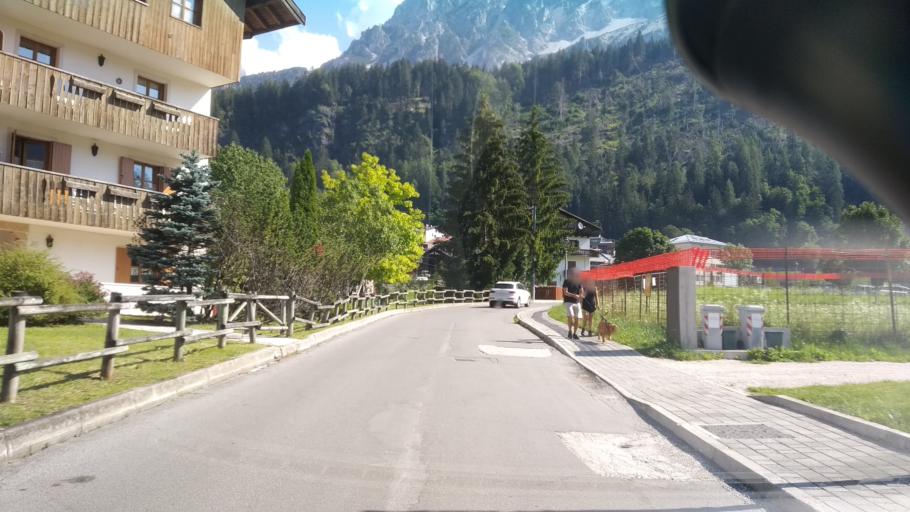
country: IT
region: Veneto
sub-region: Provincia di Belluno
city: Borca
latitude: 46.4354
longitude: 12.2187
